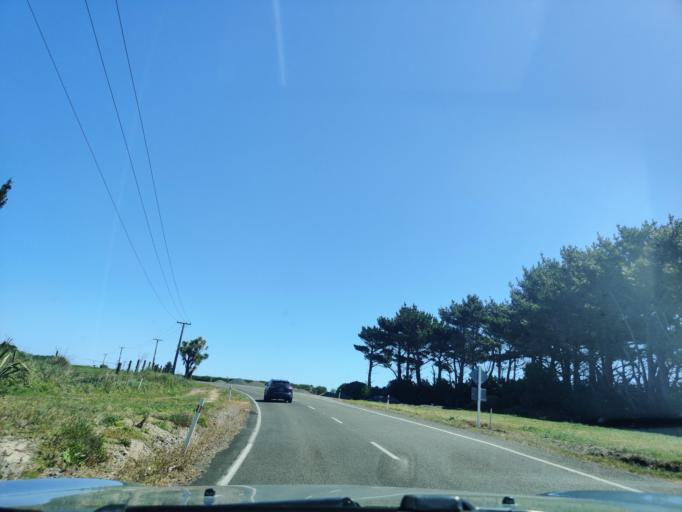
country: NZ
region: Taranaki
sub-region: South Taranaki District
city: Hawera
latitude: -39.5441
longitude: 174.0696
